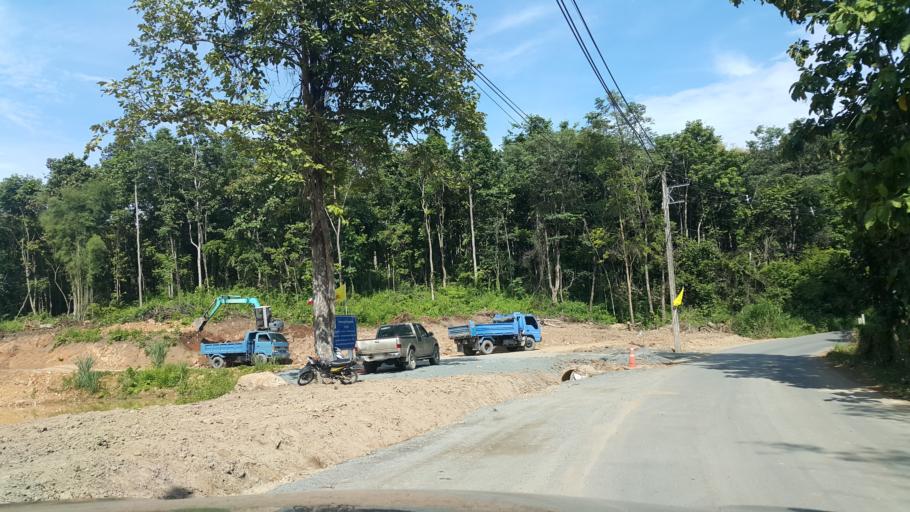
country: TH
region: Chiang Mai
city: Mae On
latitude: 18.8341
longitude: 99.1944
